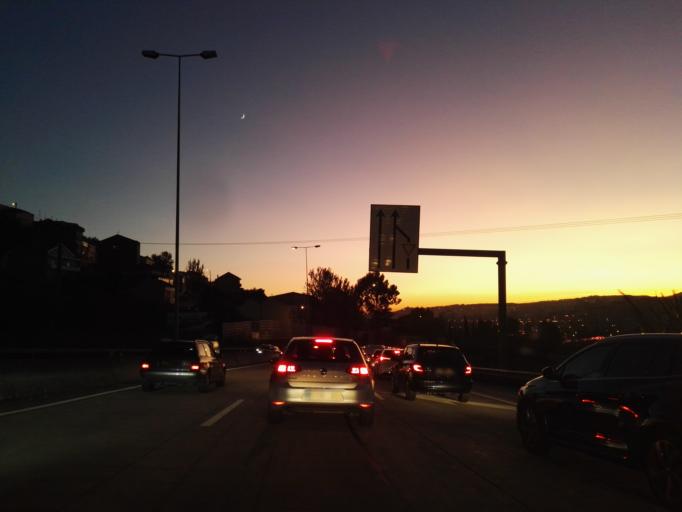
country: PT
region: Lisbon
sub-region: Odivelas
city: Povoa de Santo Adriao
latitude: 38.7974
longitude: -9.1545
